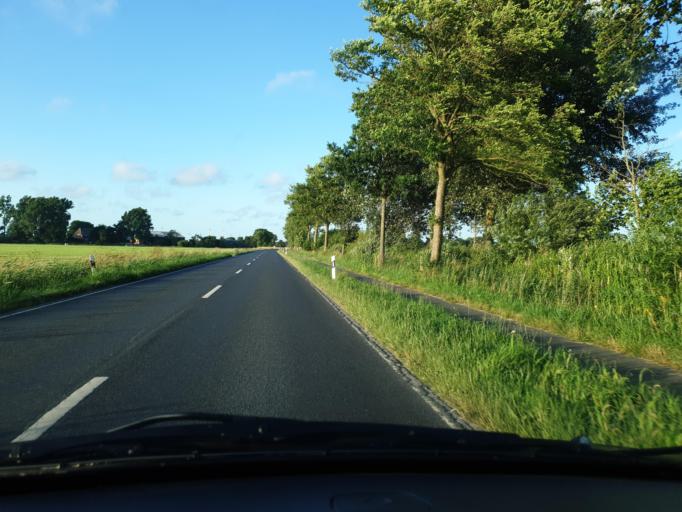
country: DE
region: Schleswig-Holstein
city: Wohrden
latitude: 54.1613
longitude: 8.9802
